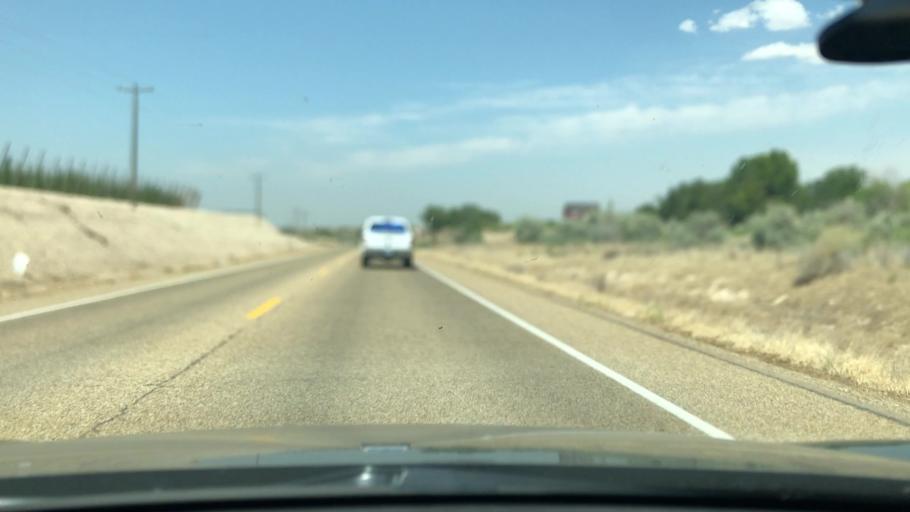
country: US
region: Idaho
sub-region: Canyon County
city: Wilder
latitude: 43.7103
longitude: -116.9119
